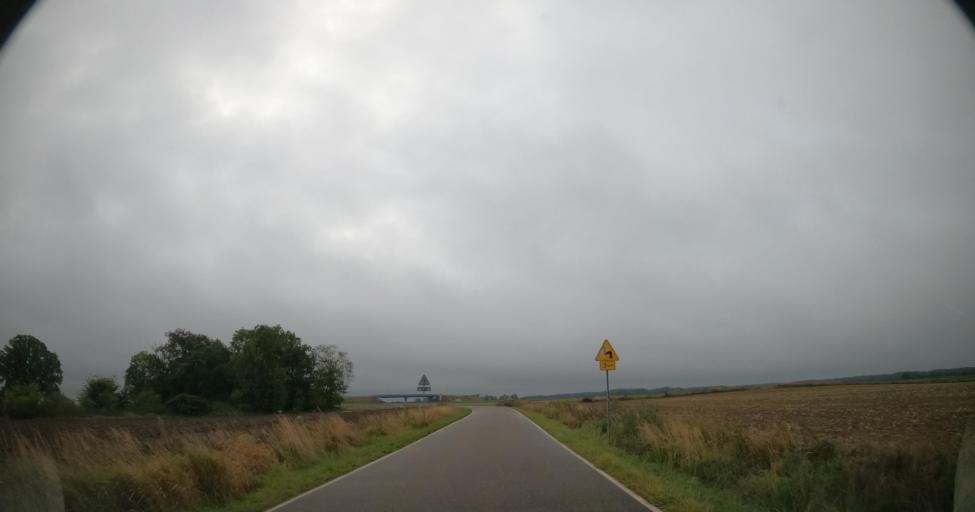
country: PL
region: West Pomeranian Voivodeship
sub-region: Powiat pyrzycki
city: Kozielice
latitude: 53.1082
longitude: 14.7645
